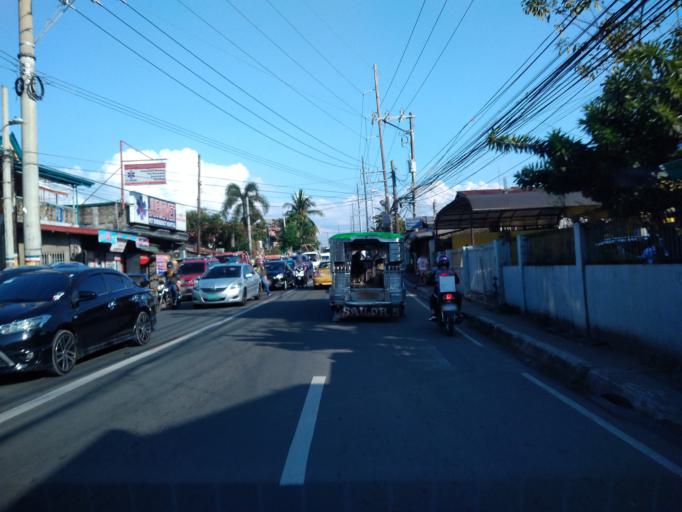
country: PH
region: Calabarzon
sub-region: Province of Laguna
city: Los Banos
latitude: 14.1812
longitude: 121.2330
